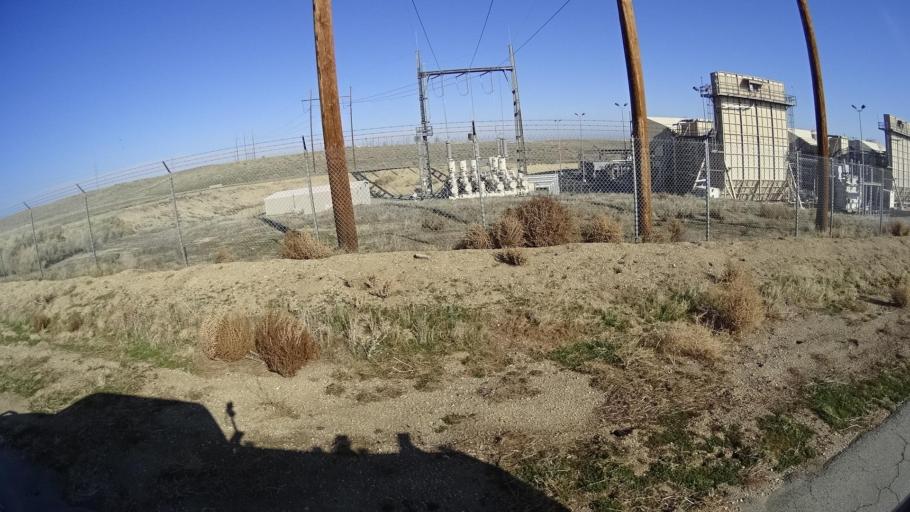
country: US
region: California
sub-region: Kern County
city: Taft Heights
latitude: 35.2270
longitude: -119.6308
